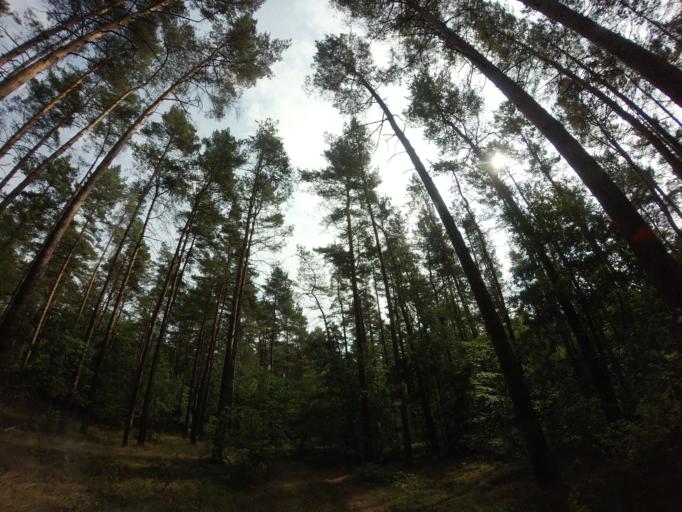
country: PL
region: West Pomeranian Voivodeship
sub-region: Powiat drawski
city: Drawsko Pomorskie
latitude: 53.4602
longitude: 15.7152
